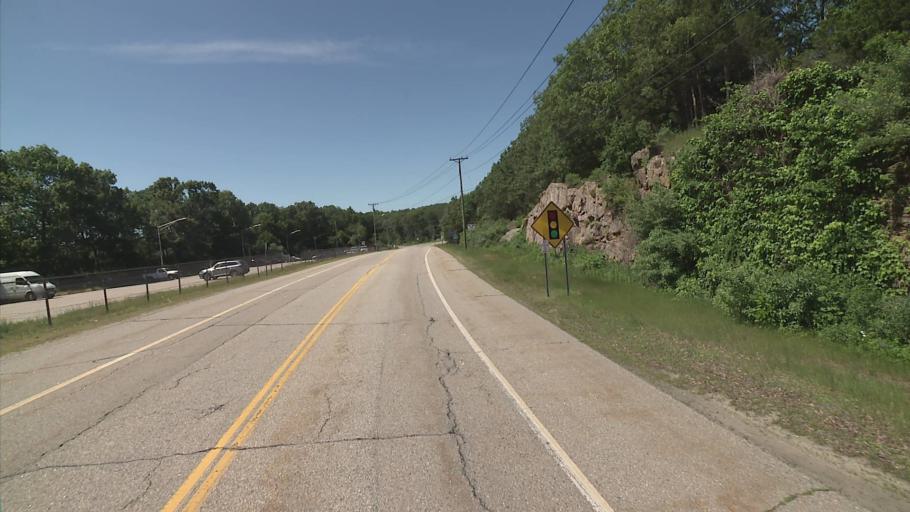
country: US
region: Connecticut
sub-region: New London County
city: Pawcatuck
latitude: 41.4144
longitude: -71.8545
